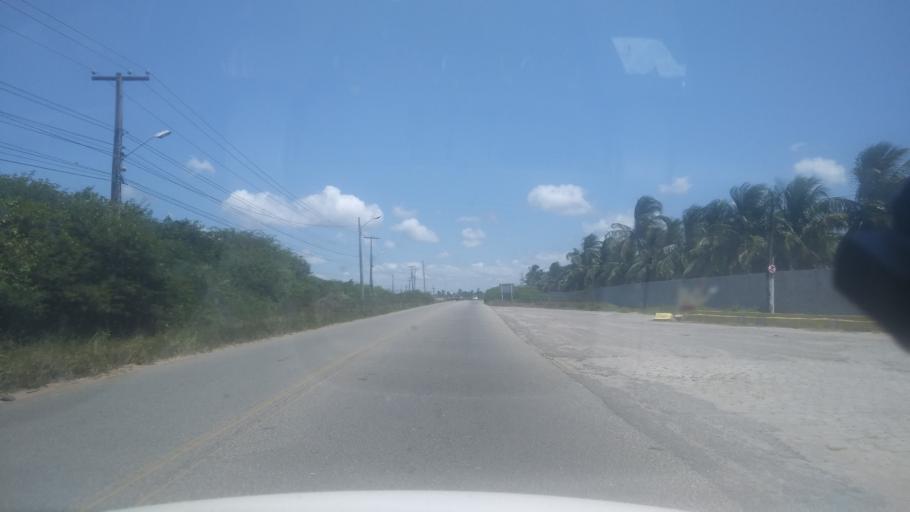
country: BR
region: Rio Grande do Norte
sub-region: Extremoz
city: Extremoz
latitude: -5.7193
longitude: -35.2778
